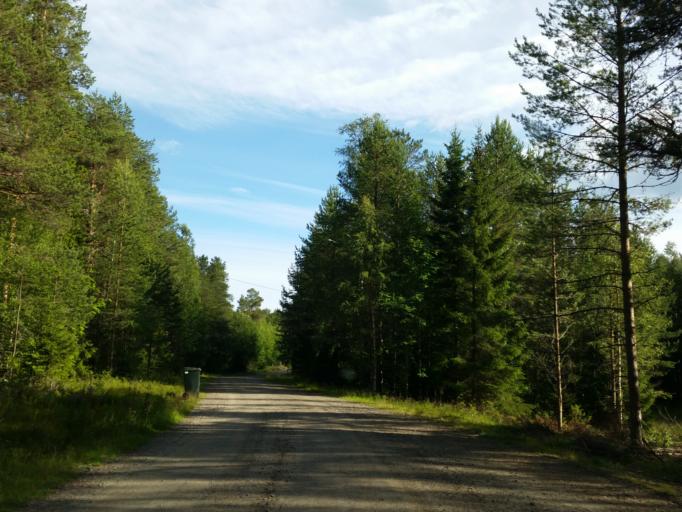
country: SE
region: Vaesterbotten
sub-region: Robertsfors Kommun
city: Robertsfors
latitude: 64.0399
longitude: 20.8500
